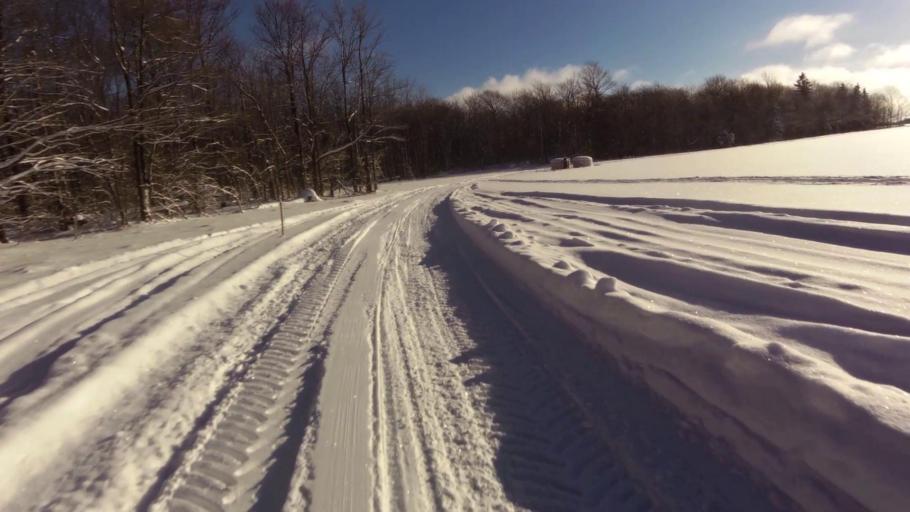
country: US
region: New York
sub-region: Chautauqua County
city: Falconer
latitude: 42.2692
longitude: -79.1931
